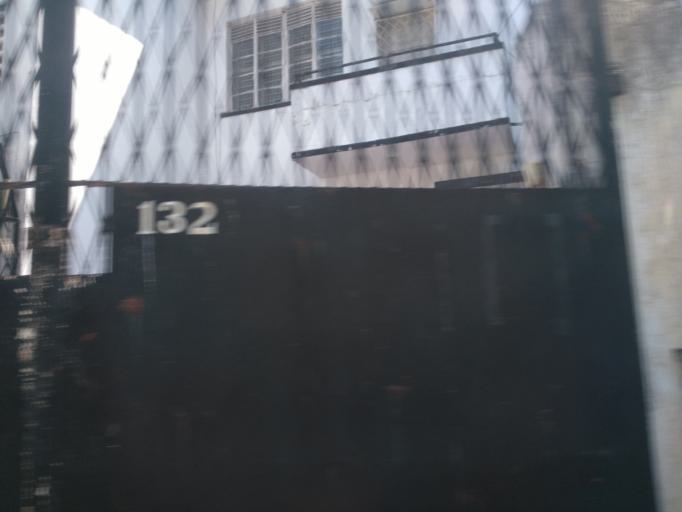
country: TZ
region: Dar es Salaam
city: Dar es Salaam
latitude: -6.8077
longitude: 39.2846
